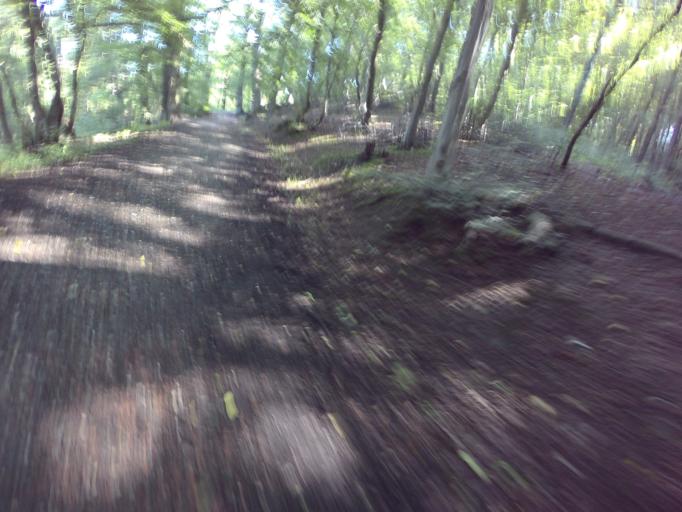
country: DE
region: North Rhine-Westphalia
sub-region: Regierungsbezirk Koln
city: Herzogenrath
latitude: 50.8396
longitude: 6.1036
